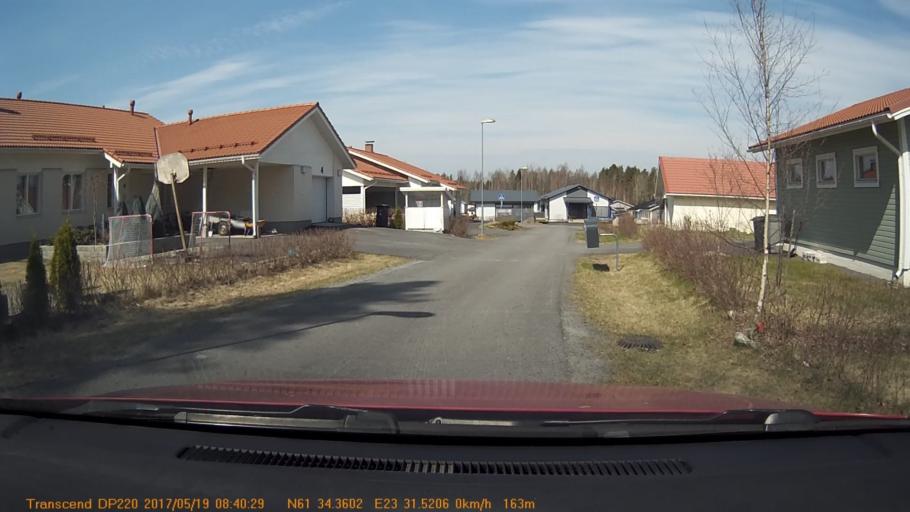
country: FI
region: Pirkanmaa
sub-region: Tampere
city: Yloejaervi
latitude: 61.5727
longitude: 23.5254
